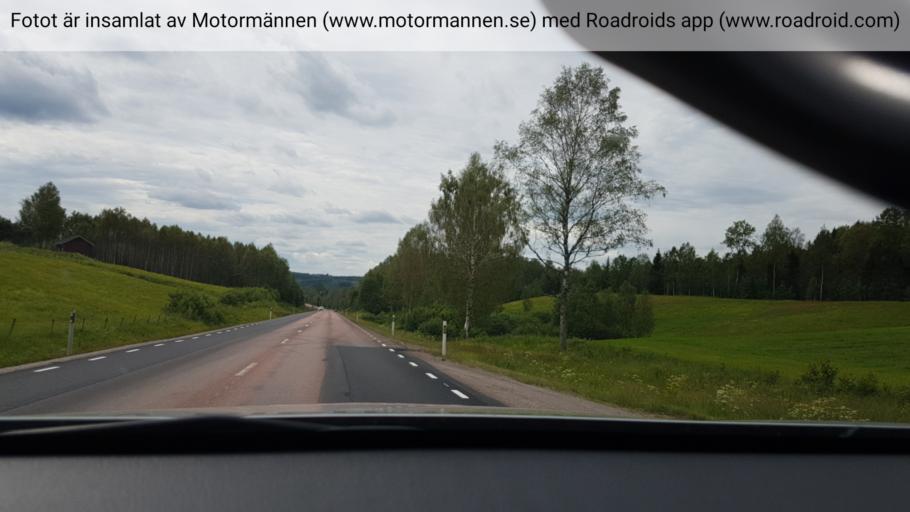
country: SE
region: Vaermland
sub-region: Torsby Kommun
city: Torsby
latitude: 60.2513
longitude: 13.0165
